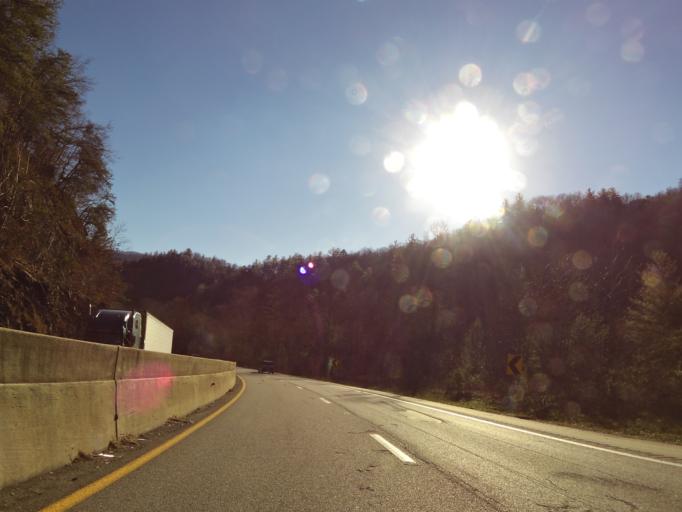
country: US
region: North Carolina
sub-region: Haywood County
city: Cove Creek
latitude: 35.7398
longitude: -83.0355
